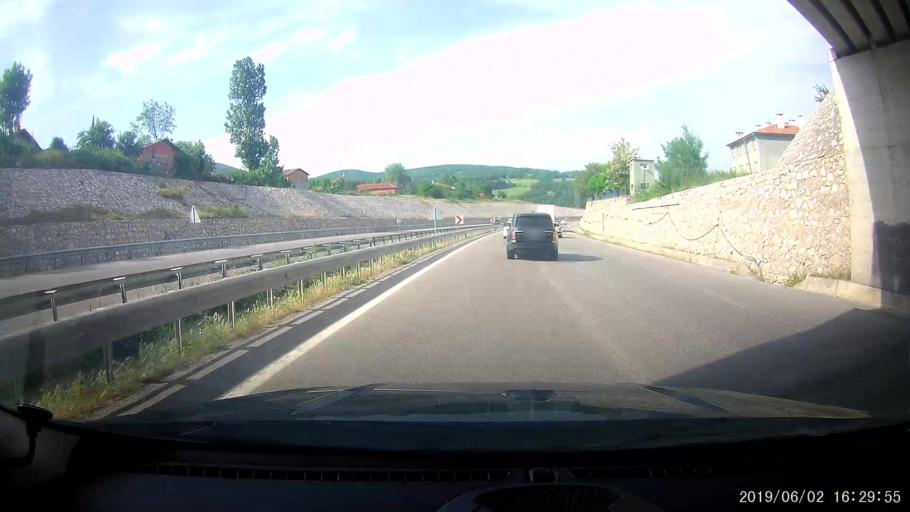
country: TR
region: Samsun
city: Ladik
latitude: 41.0198
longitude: 35.8733
